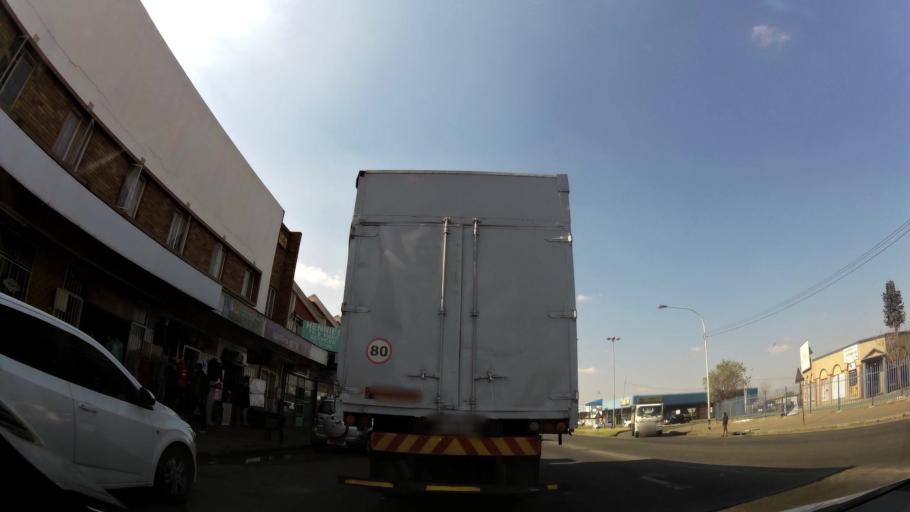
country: ZA
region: Gauteng
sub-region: Ekurhuleni Metropolitan Municipality
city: Boksburg
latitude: -26.2087
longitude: 28.2530
